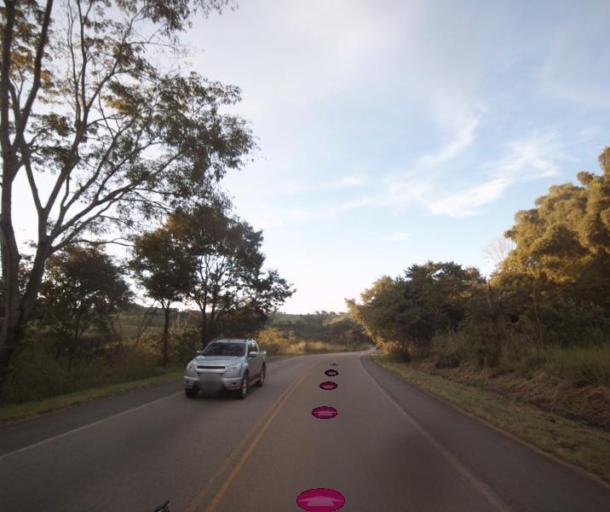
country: BR
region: Goias
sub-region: Abadiania
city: Abadiania
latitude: -16.1276
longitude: -48.8951
